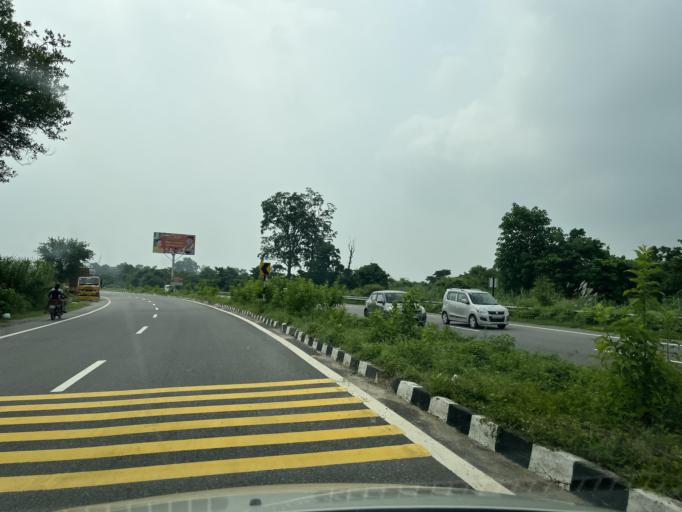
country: IN
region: Uttarakhand
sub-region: Dehradun
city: Raiwala
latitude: 30.0584
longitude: 78.2142
